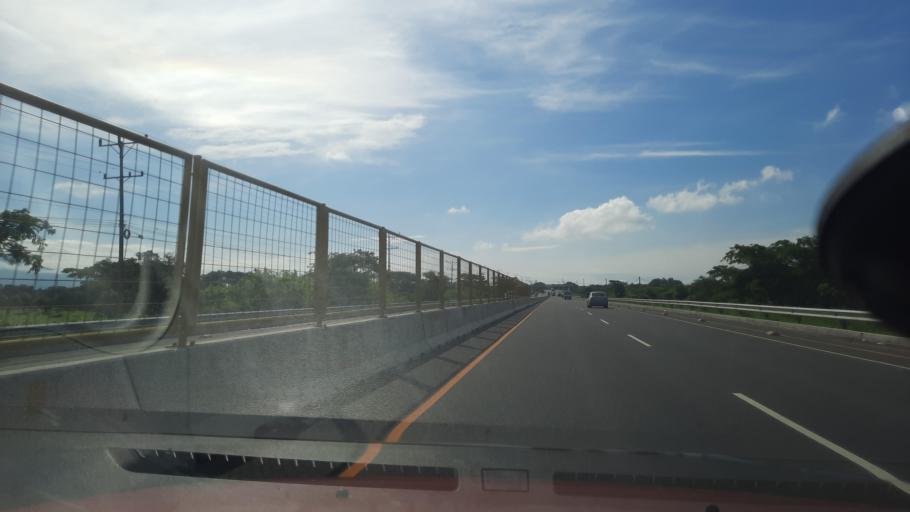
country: SV
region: La Paz
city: El Rosario
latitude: 13.4655
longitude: -89.0209
